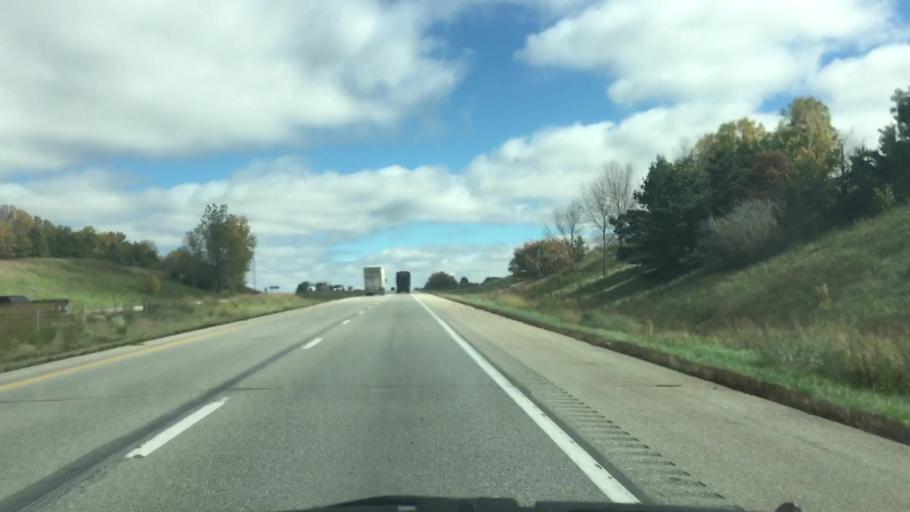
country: US
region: Iowa
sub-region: Poweshiek County
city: Grinnell
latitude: 41.6951
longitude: -92.8168
